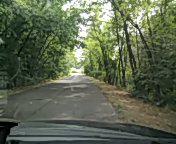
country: HU
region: Hajdu-Bihar
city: Hajdusamson
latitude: 47.5148
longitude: 21.7350
